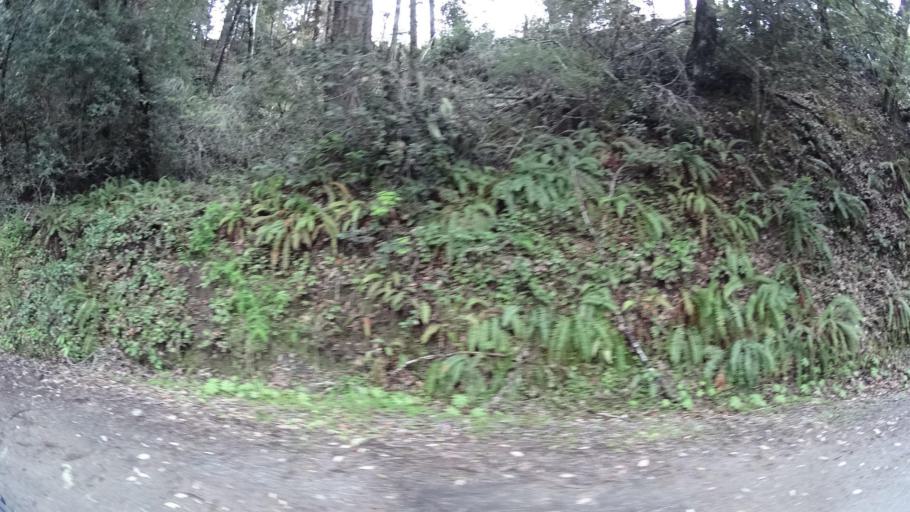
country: US
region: California
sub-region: Humboldt County
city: Blue Lake
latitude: 40.8690
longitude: -123.9027
